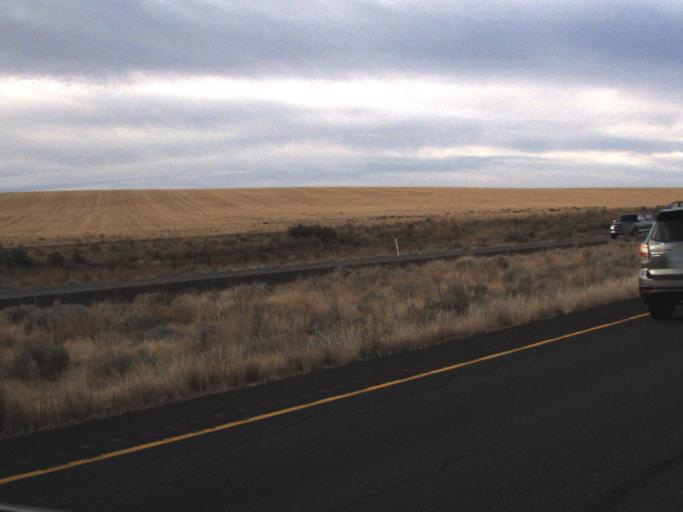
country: US
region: Washington
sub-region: Franklin County
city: Connell
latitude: 46.7866
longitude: -118.7573
